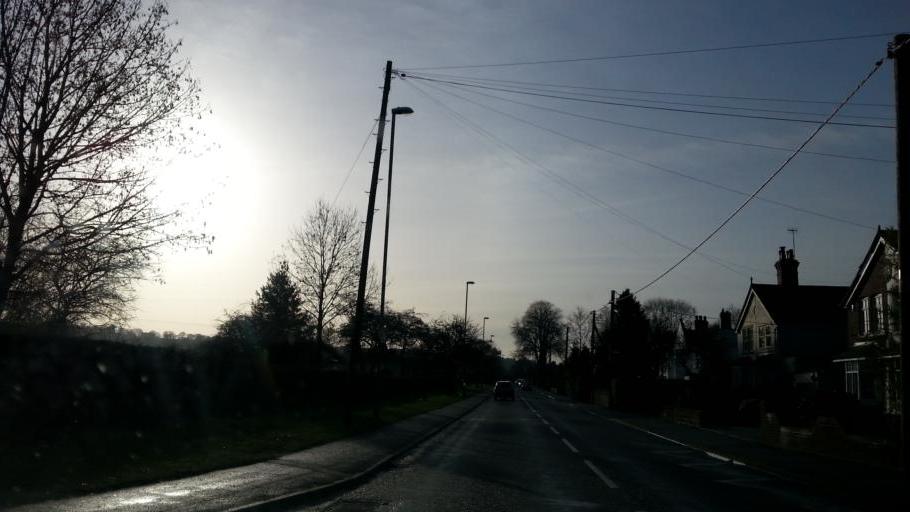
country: GB
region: England
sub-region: Staffordshire
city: Cheddleton
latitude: 53.0729
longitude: -2.1155
